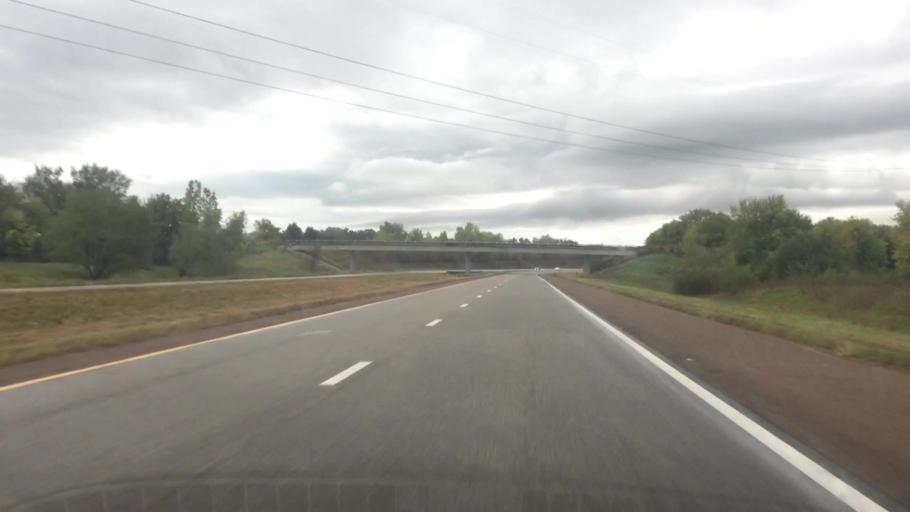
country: US
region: Kansas
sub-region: Miami County
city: Paola
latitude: 38.5871
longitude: -94.8354
